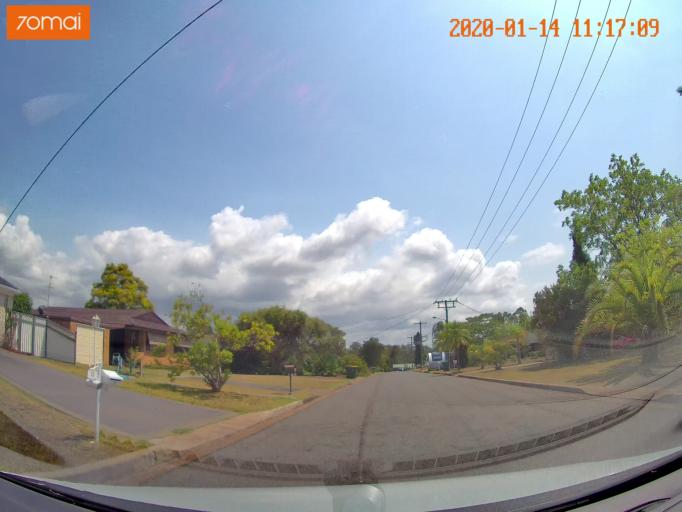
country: AU
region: New South Wales
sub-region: Lake Macquarie Shire
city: Cooranbong
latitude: -33.0956
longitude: 151.4618
